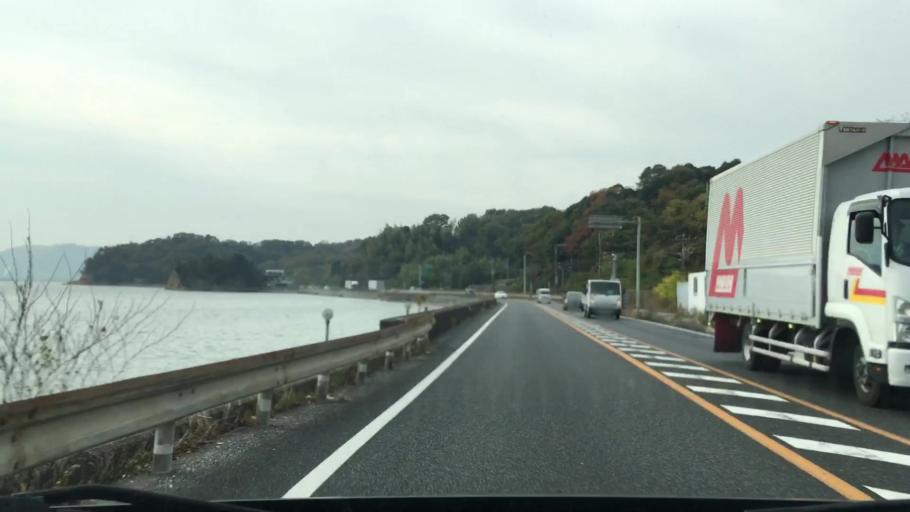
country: JP
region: Hiroshima
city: Ono-hara
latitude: 34.2703
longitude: 132.2548
